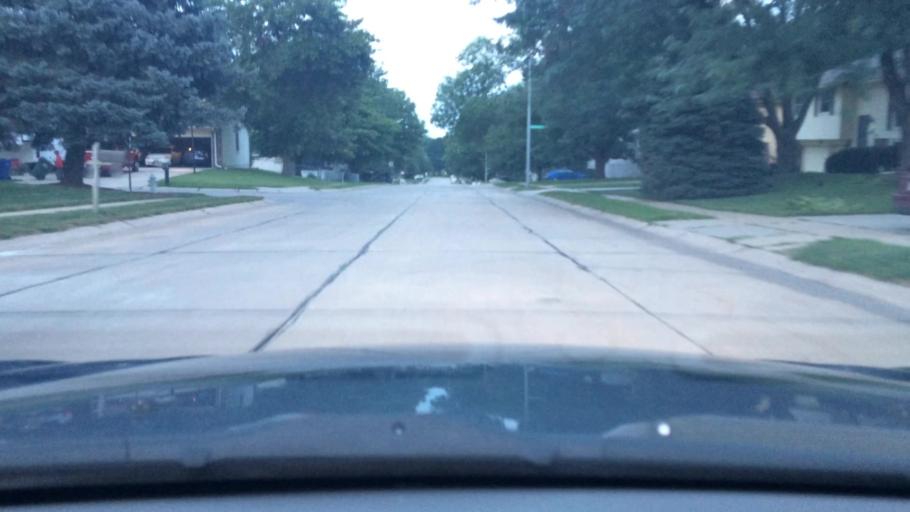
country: US
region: Nebraska
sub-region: Douglas County
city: Ralston
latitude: 41.1839
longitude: -96.0571
